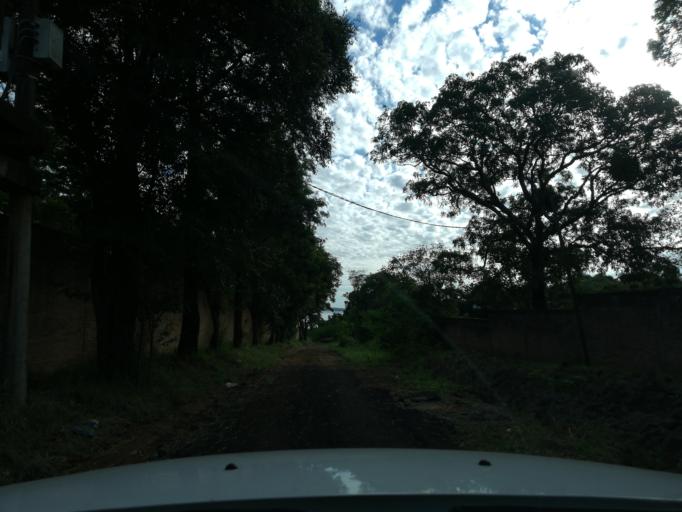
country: AR
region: Misiones
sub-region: Departamento de Capital
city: Posadas
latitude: -27.3553
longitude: -55.9339
